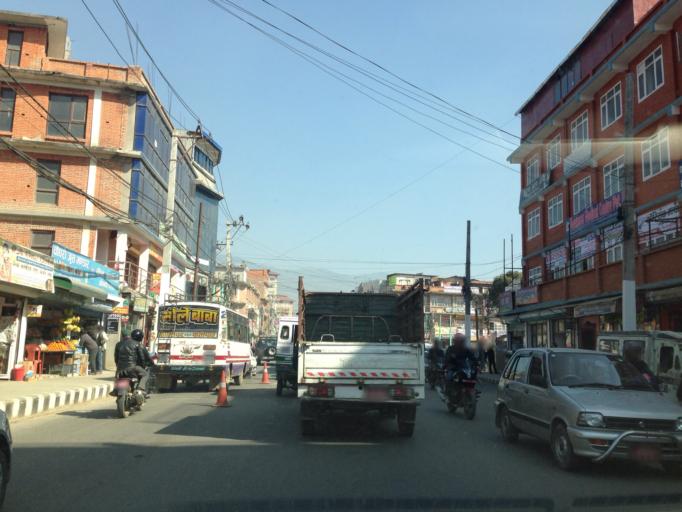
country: NP
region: Central Region
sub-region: Bagmati Zone
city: Kathmandu
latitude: 27.7395
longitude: 85.3367
